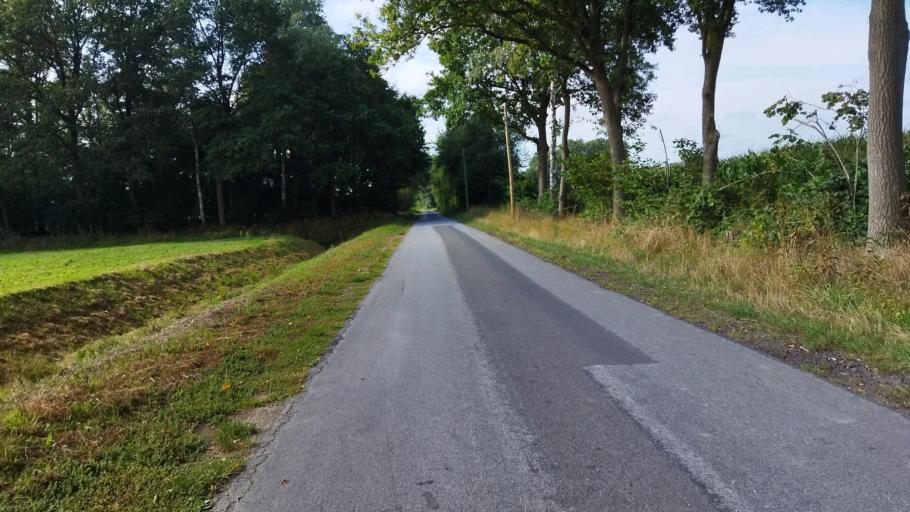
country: DE
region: North Rhine-Westphalia
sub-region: Regierungsbezirk Munster
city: Sassenberg
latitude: 52.0004
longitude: 8.0172
